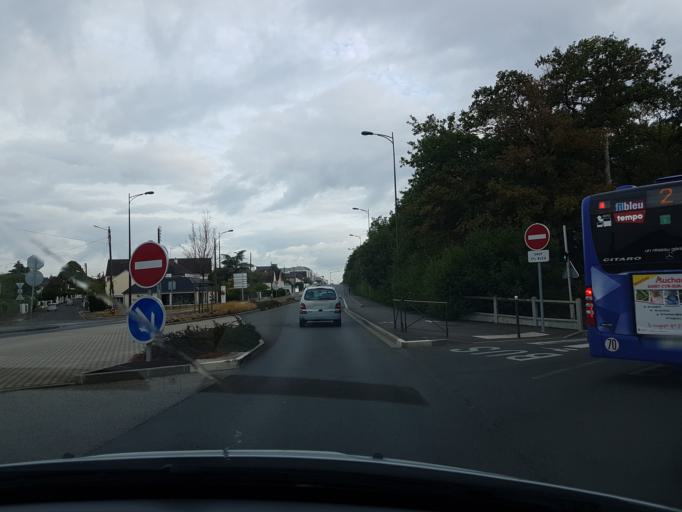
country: FR
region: Centre
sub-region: Departement d'Indre-et-Loire
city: Chambray-les-Tours
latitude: 47.3510
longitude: 0.7004
